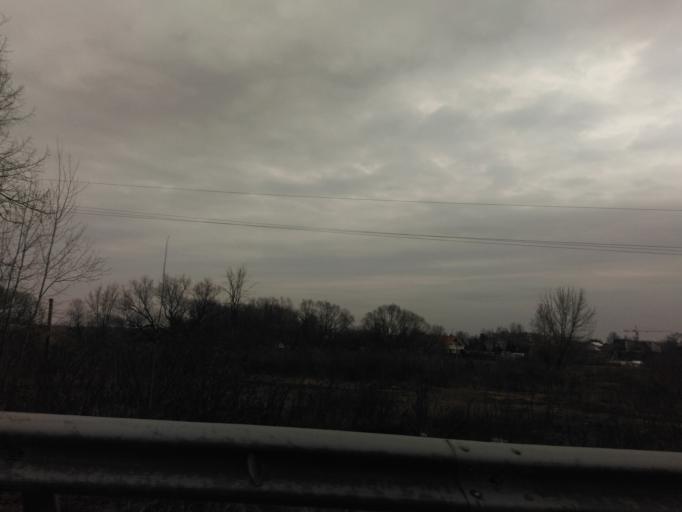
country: RU
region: Moskovskaya
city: Nikolina Gora
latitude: 55.7231
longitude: 37.0648
